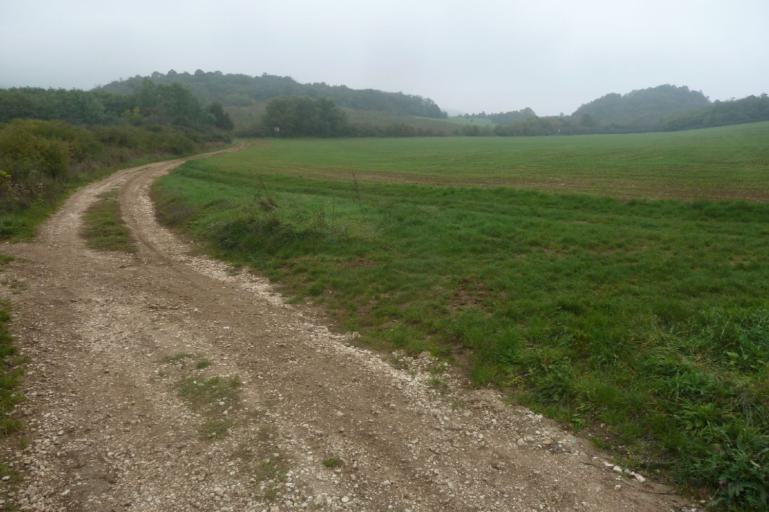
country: HU
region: Nograd
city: Romhany
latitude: 47.8389
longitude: 19.2814
